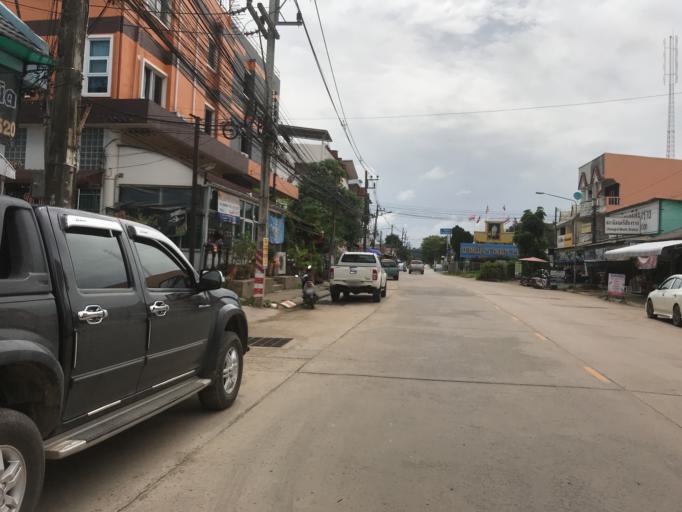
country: TH
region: Chiang Rai
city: Chiang Rai
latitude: 19.9033
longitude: 99.8144
